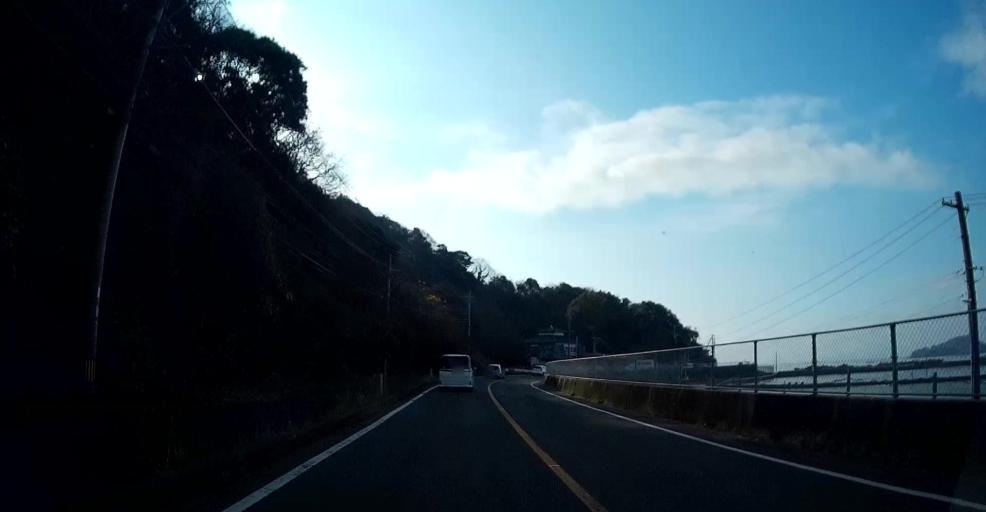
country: JP
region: Kumamoto
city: Yatsushiro
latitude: 32.5683
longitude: 130.4139
